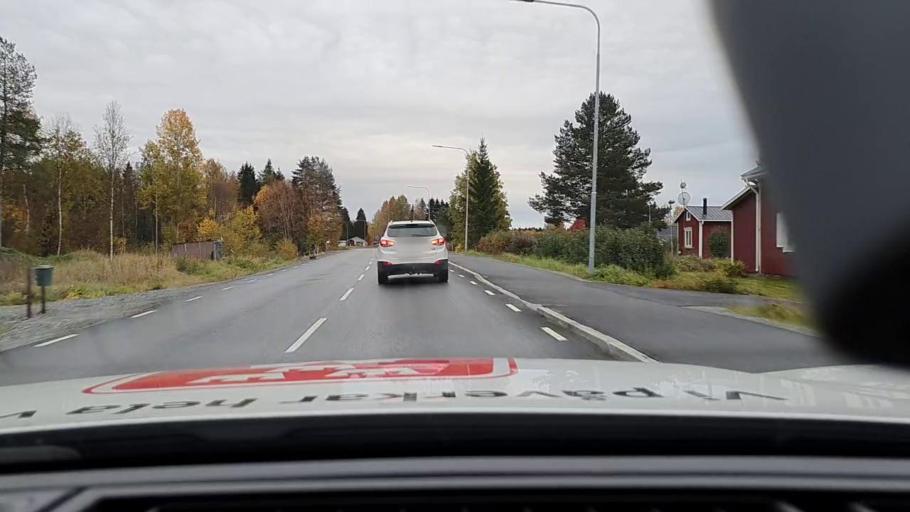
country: SE
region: Norrbotten
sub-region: Bodens Kommun
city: Saevast
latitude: 65.7742
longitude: 21.6961
